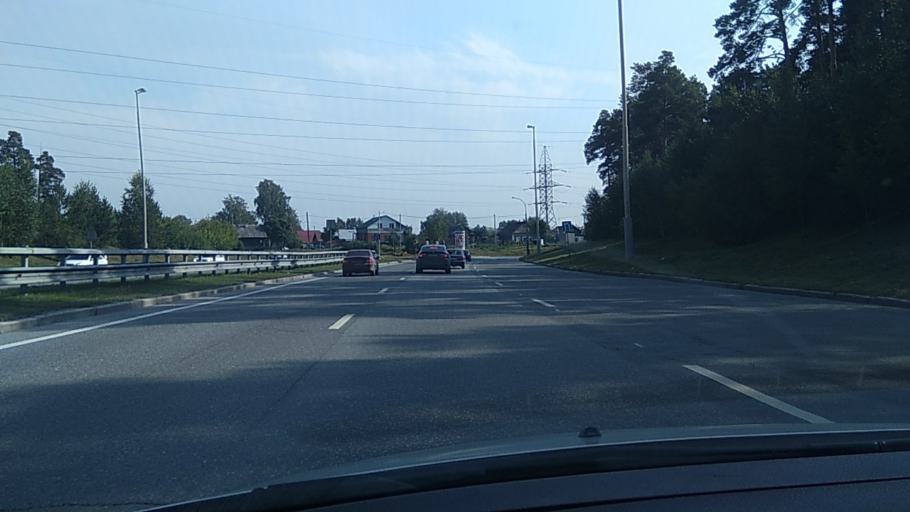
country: RU
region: Sverdlovsk
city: Yekaterinburg
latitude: 56.8862
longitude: 60.5519
